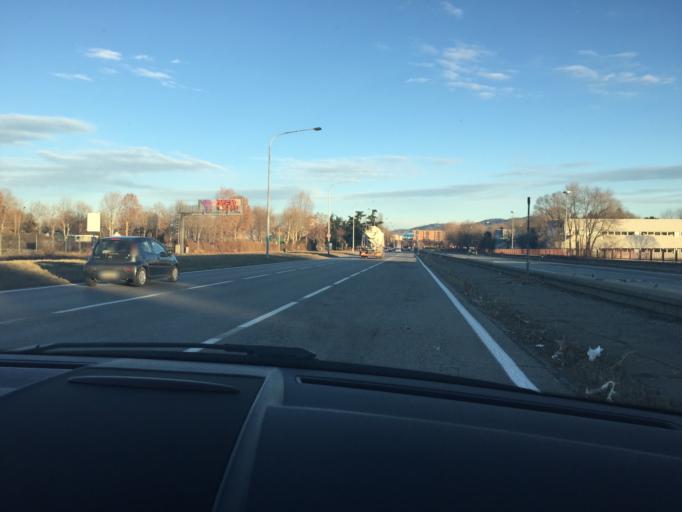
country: IT
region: Piedmont
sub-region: Provincia di Torino
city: Gerbido
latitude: 45.0511
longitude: 7.6097
